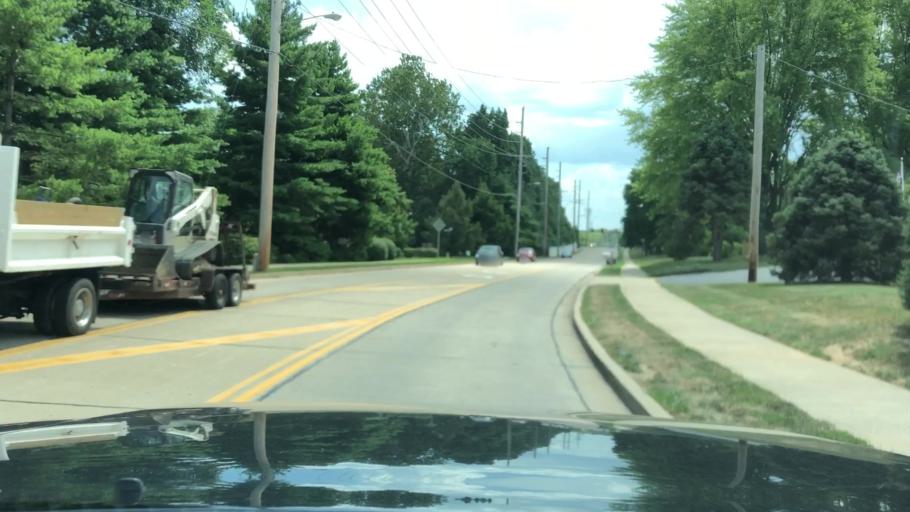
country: US
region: Missouri
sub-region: Saint Charles County
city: Saint Charles
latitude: 38.8058
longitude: -90.5355
